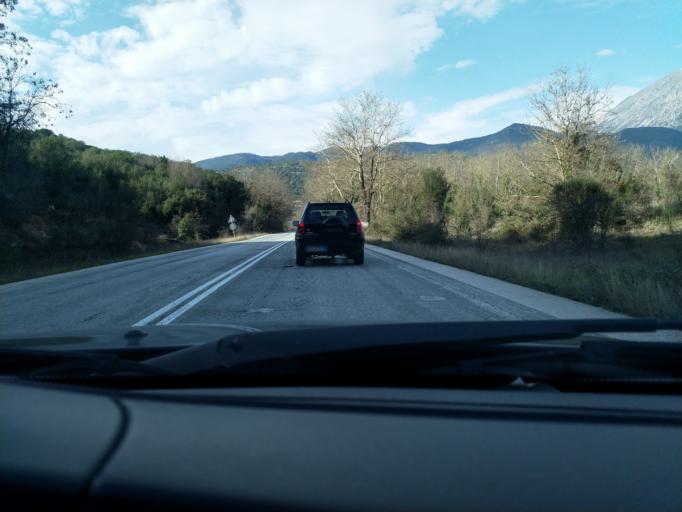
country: GR
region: Epirus
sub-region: Nomos Ioanninon
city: Agia Kyriaki
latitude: 39.4521
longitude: 20.8726
